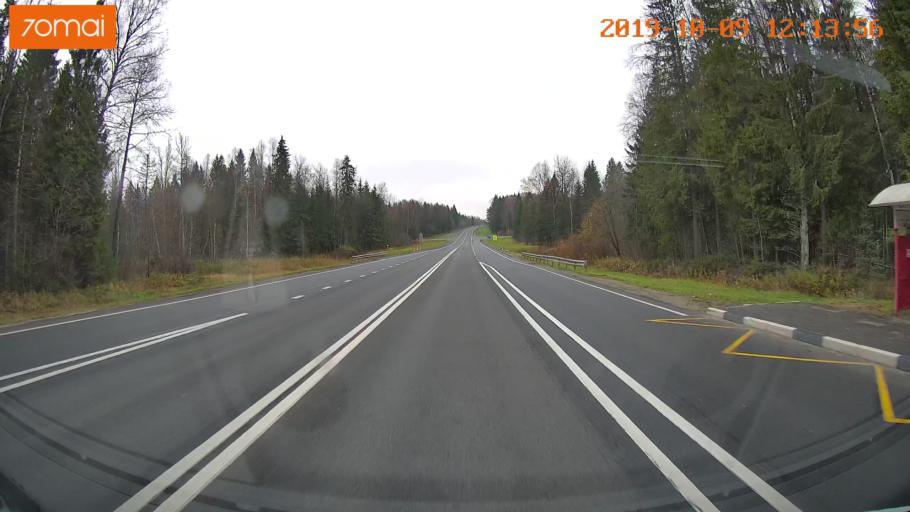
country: RU
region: Jaroslavl
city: Prechistoye
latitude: 58.5028
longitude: 40.3424
